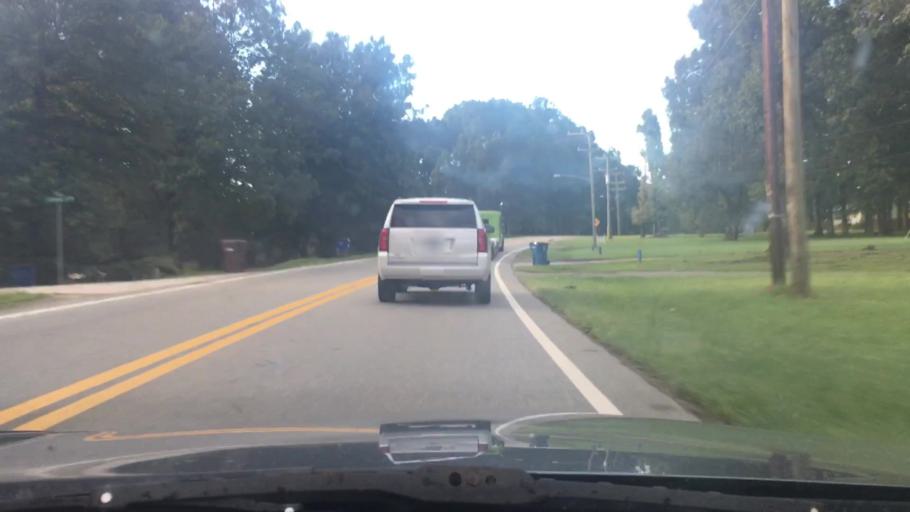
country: US
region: North Carolina
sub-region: Alamance County
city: Green Level
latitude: 36.1317
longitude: -79.3450
